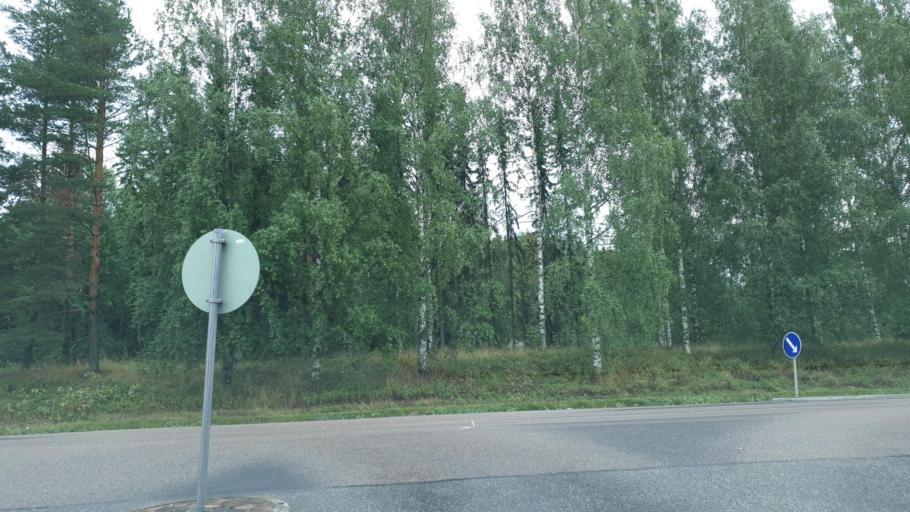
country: FI
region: Paijanne Tavastia
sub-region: Lahti
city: Lahti
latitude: 60.9602
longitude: 25.6580
